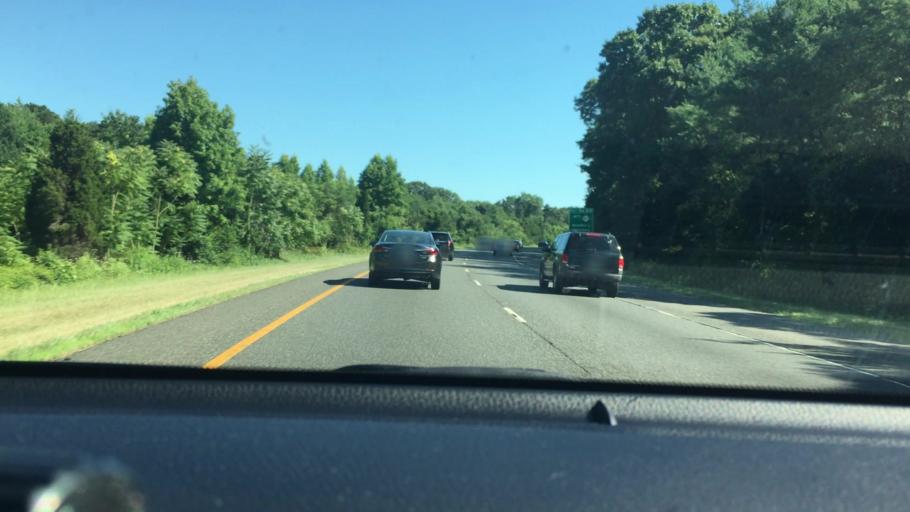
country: US
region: New Jersey
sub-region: Camden County
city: Blackwood
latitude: 39.8072
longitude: -75.1051
